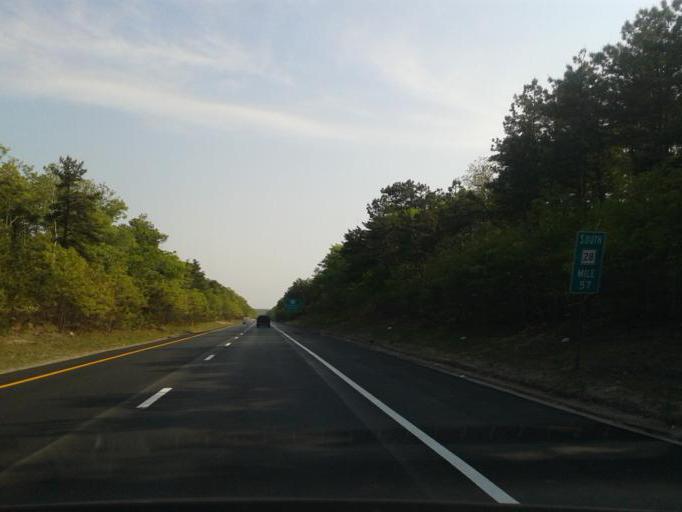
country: US
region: Massachusetts
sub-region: Barnstable County
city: North Falmouth
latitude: 41.6633
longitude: -70.6003
